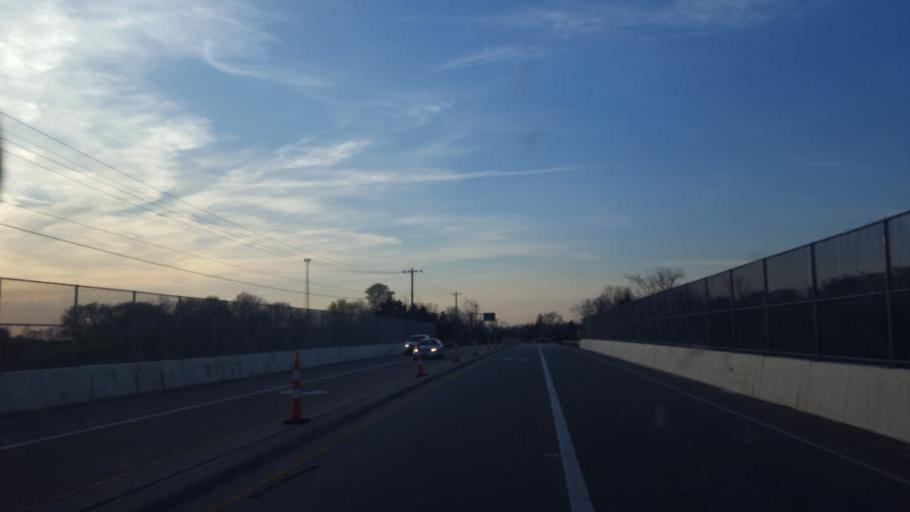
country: US
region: Ohio
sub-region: Warren County
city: Lebanon
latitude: 39.4126
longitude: -84.1525
